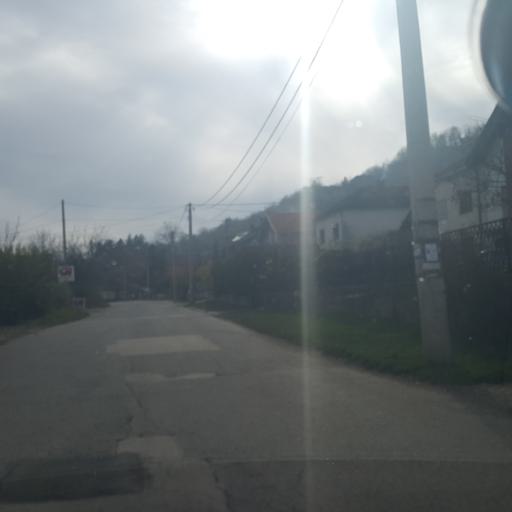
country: RS
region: Central Serbia
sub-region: Zajecarski Okrug
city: Knjazevac
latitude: 43.5739
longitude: 22.2476
